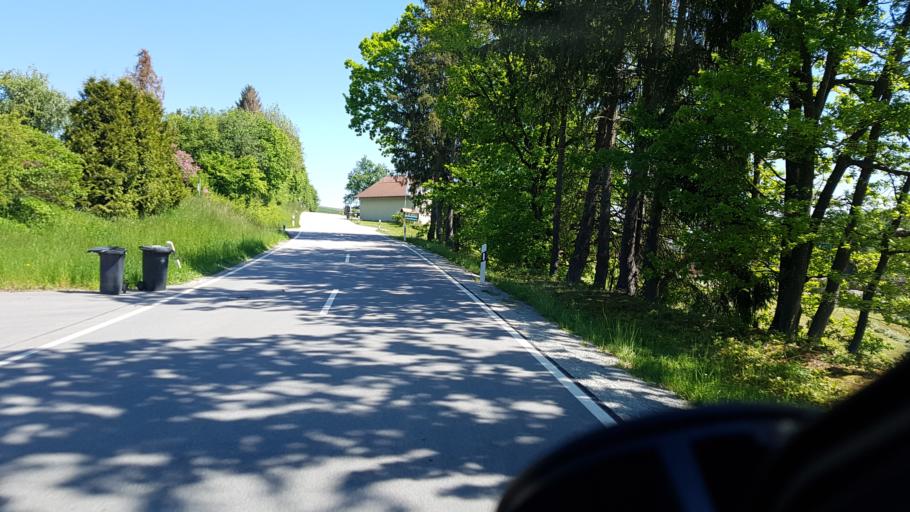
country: DE
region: Bavaria
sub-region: Lower Bavaria
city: Postmunster
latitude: 48.3744
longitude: 12.8999
